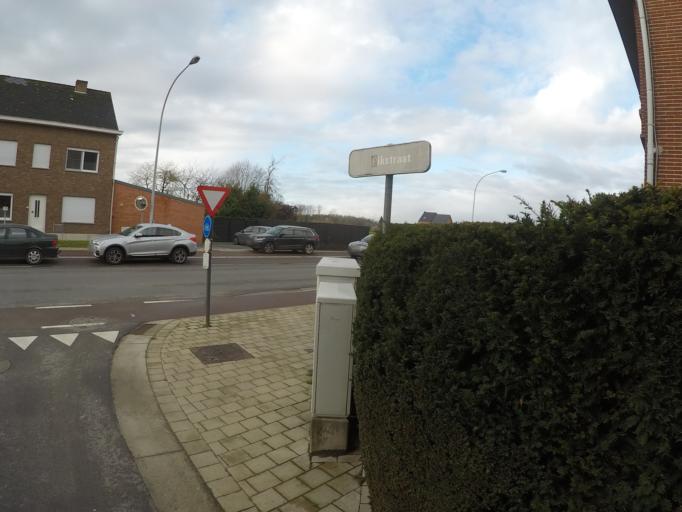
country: BE
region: Flanders
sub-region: Provincie Vlaams-Brabant
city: Londerzeel
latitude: 51.0149
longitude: 4.2948
